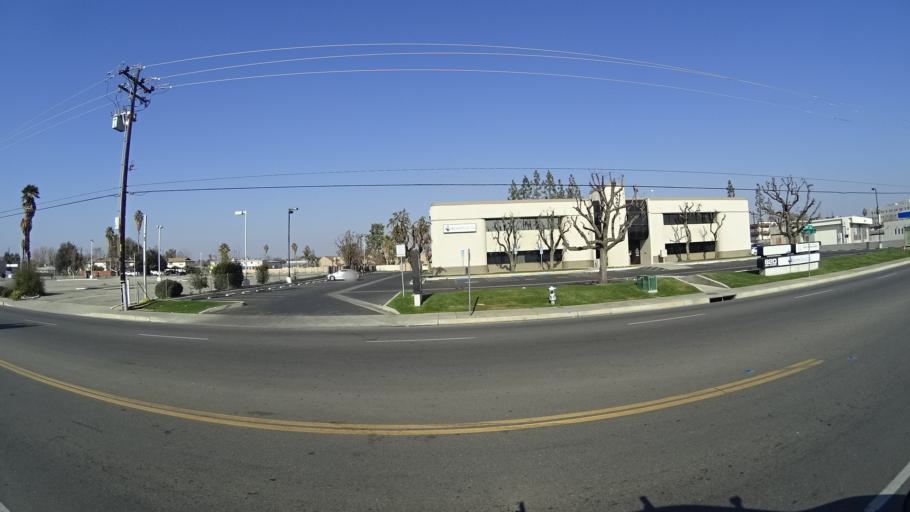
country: US
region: California
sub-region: Kern County
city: Bakersfield
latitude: 35.3904
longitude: -119.0120
